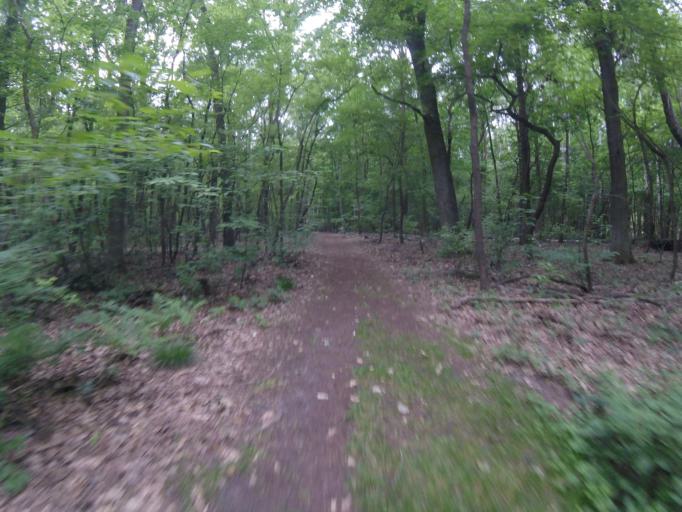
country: DE
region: Brandenburg
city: Bestensee
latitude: 52.2401
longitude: 13.6526
